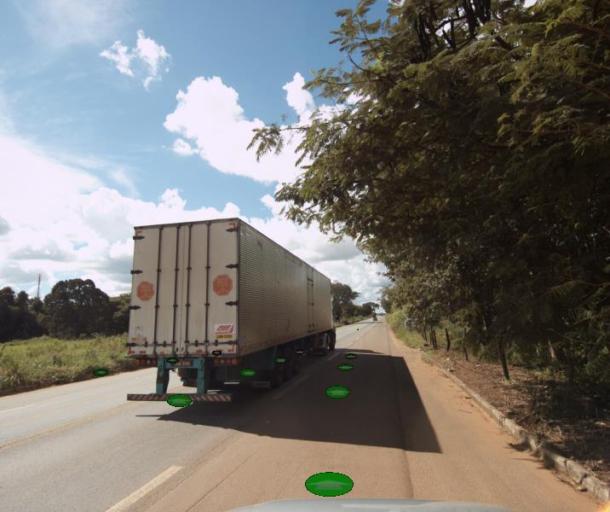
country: BR
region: Goias
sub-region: Porangatu
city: Porangatu
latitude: -13.4404
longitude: -49.1326
